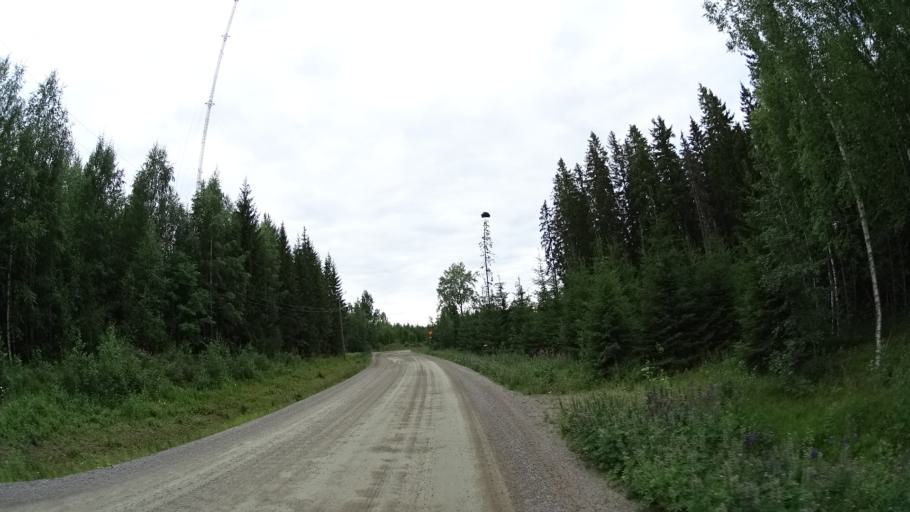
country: FI
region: Satakunta
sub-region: Pohjois-Satakunta
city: Jaemijaervi
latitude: 61.7768
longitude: 22.8620
